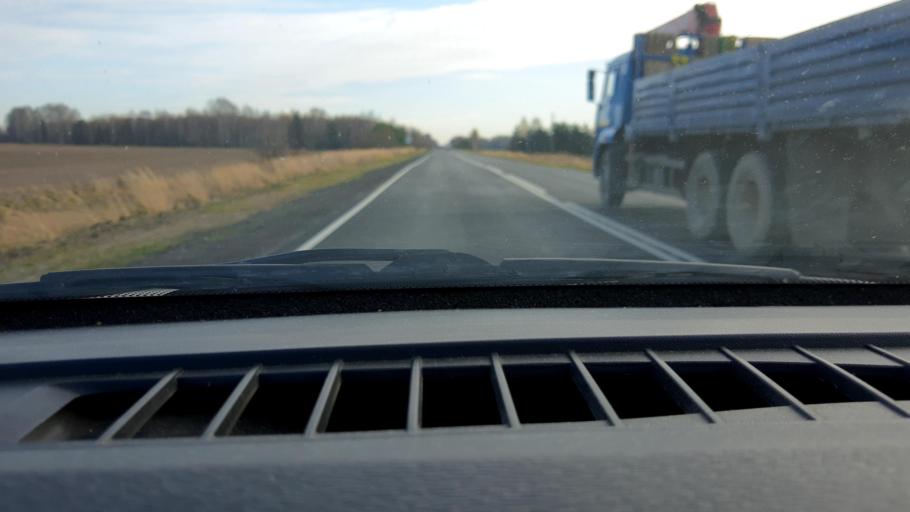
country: RU
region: Nizjnij Novgorod
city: Novaya Balakhna
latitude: 56.5961
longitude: 43.6458
